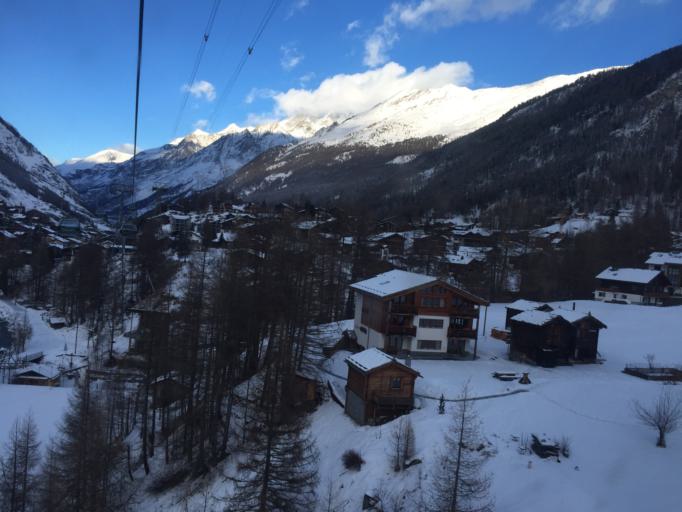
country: CH
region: Valais
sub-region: Visp District
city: Zermatt
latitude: 46.0113
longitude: 7.7398
